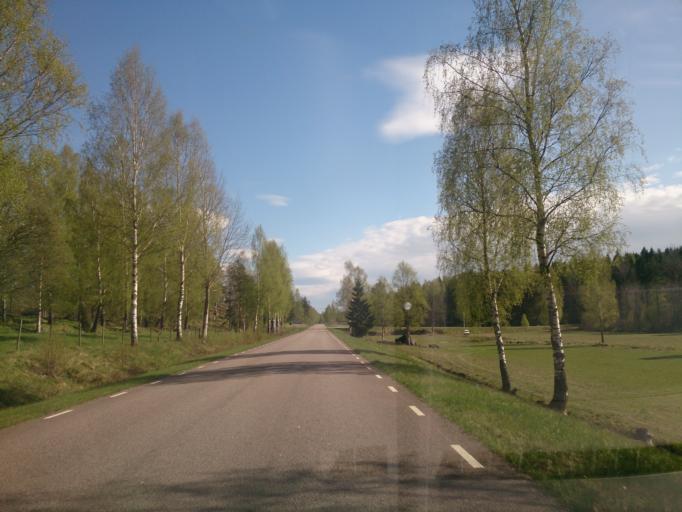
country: SE
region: OEstergoetland
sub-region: Linkopings Kommun
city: Ljungsbro
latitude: 58.5924
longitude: 15.5006
